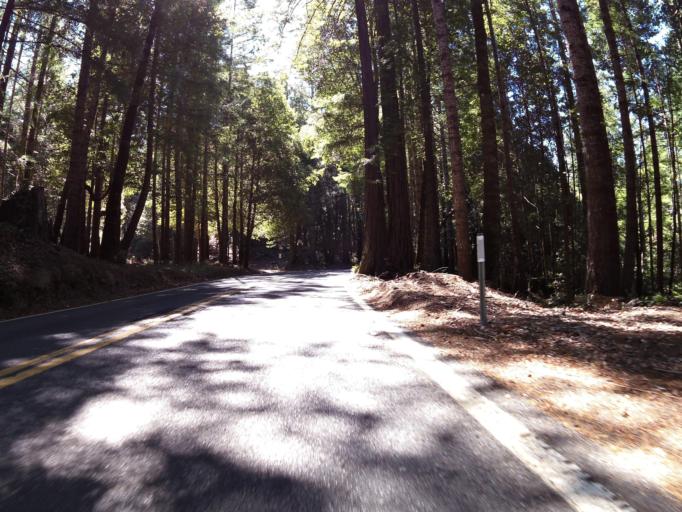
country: US
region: California
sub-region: Humboldt County
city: Redway
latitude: 39.8373
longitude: -123.7725
